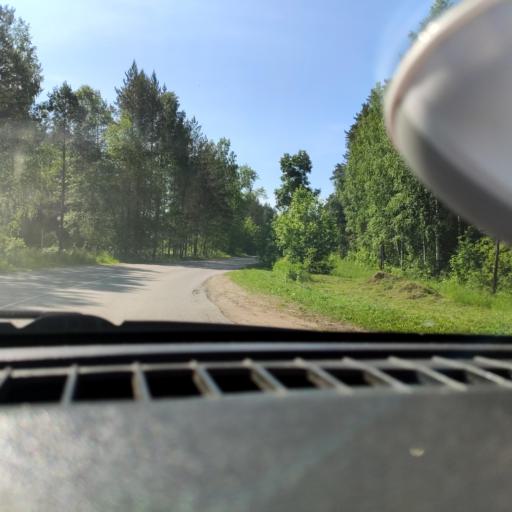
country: RU
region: Perm
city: Overyata
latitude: 57.9976
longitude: 55.8809
